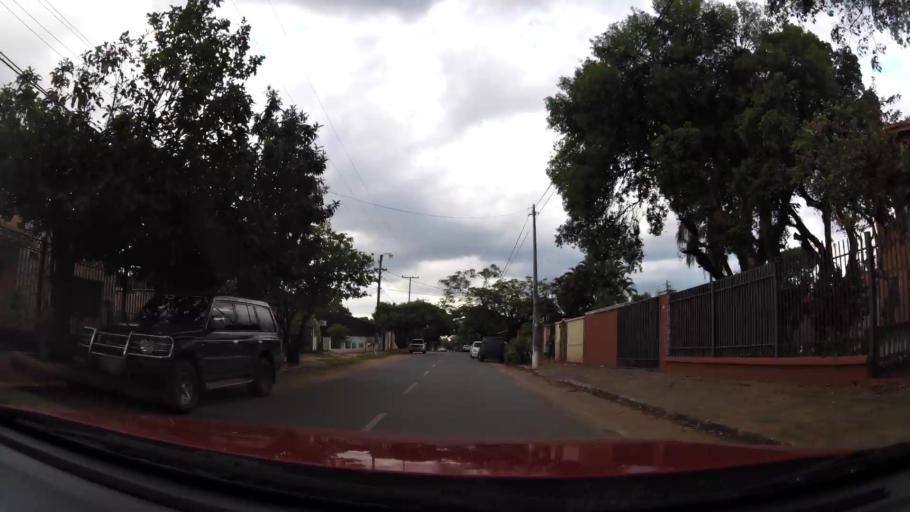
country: PY
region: Central
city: Fernando de la Mora
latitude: -25.3327
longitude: -57.5565
